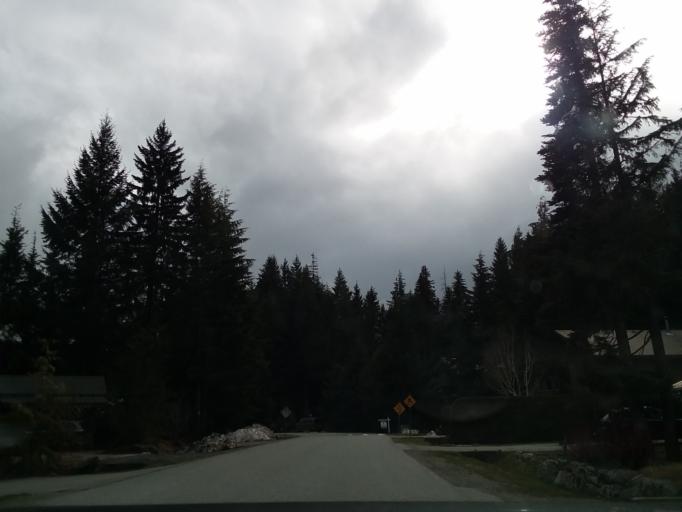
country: CA
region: British Columbia
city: Whistler
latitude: 50.1287
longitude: -122.9679
